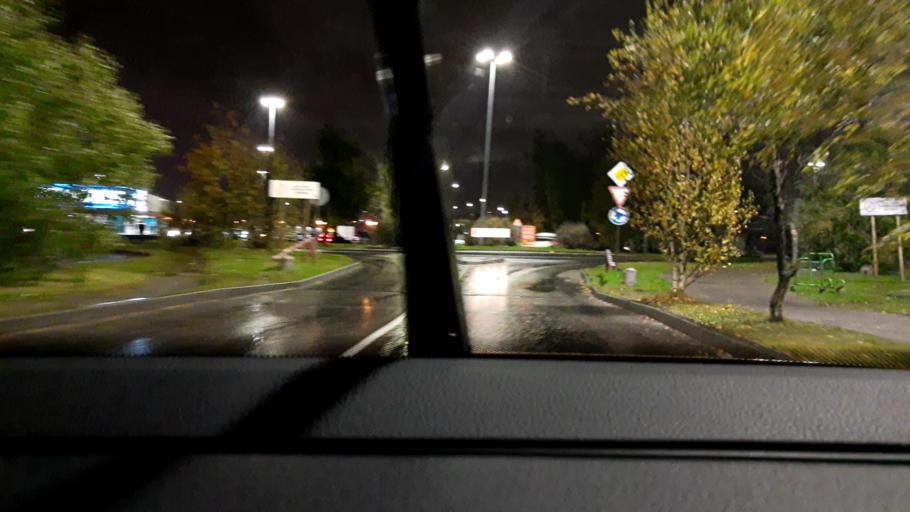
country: RU
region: Moscow
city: Lianozovo
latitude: 55.9140
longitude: 37.5747
